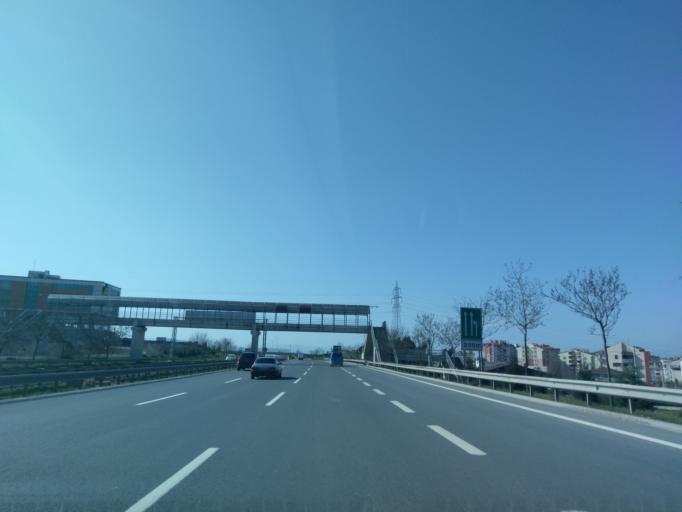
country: TR
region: Kocaeli
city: Balcik
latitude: 40.8612
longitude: 29.3805
